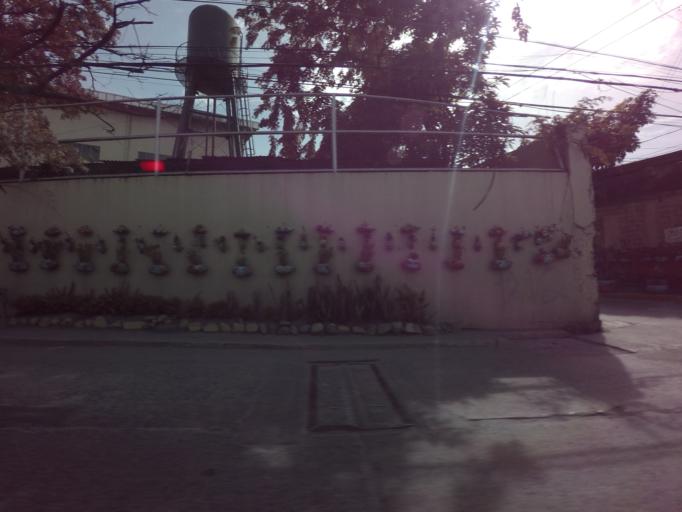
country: PH
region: Calabarzon
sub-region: Province of Rizal
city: Pateros
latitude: 14.5490
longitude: 121.0865
